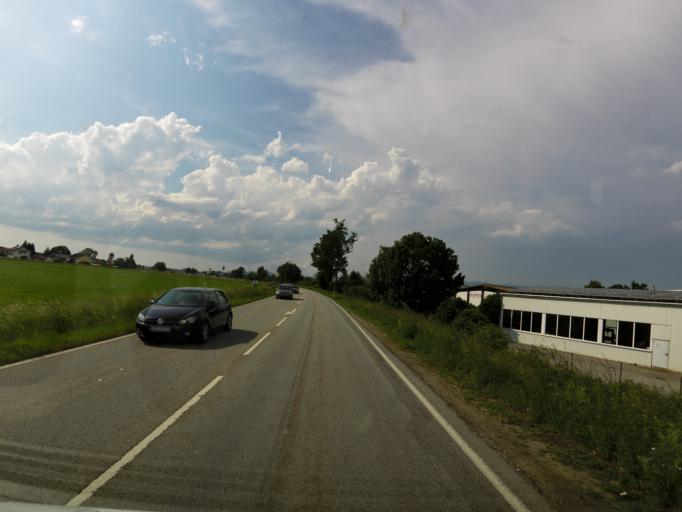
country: DE
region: Bavaria
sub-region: Lower Bavaria
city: Hengersberg
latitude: 48.7623
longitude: 13.0513
